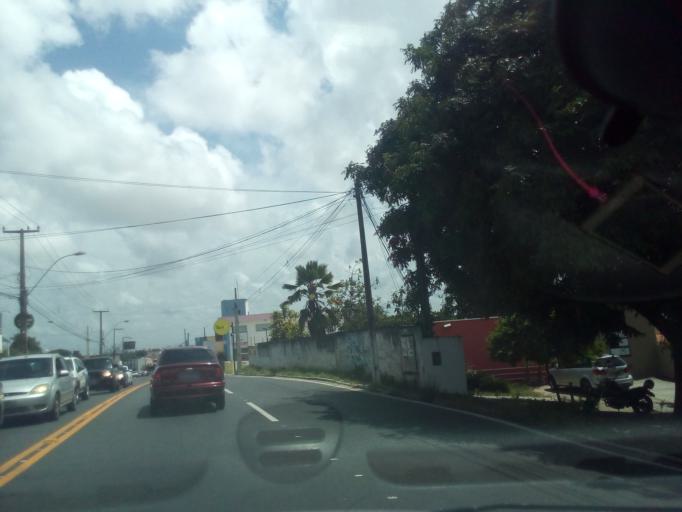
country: BR
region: Rio Grande do Norte
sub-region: Natal
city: Natal
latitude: -5.8594
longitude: -35.2057
